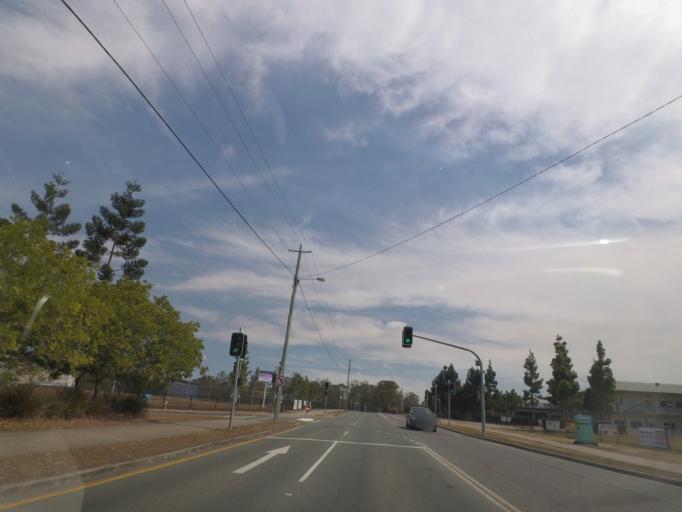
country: AU
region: Queensland
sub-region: Brisbane
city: Sunnybank Hills
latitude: -27.6384
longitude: 153.0571
